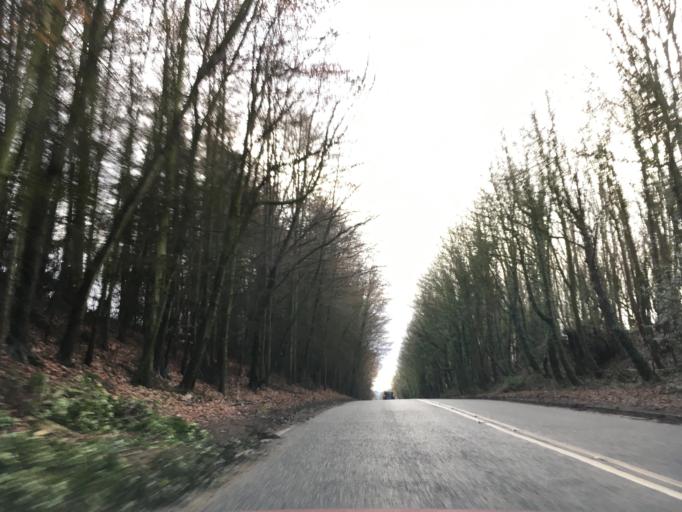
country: GB
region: England
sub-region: Gloucestershire
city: Charlton Kings
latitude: 51.8583
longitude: -2.0474
